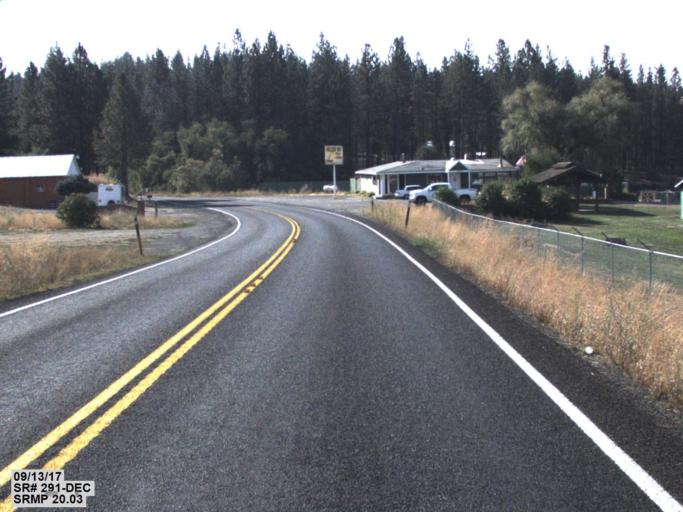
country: US
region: Washington
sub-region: Spokane County
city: Deer Park
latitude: 47.8810
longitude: -117.6572
